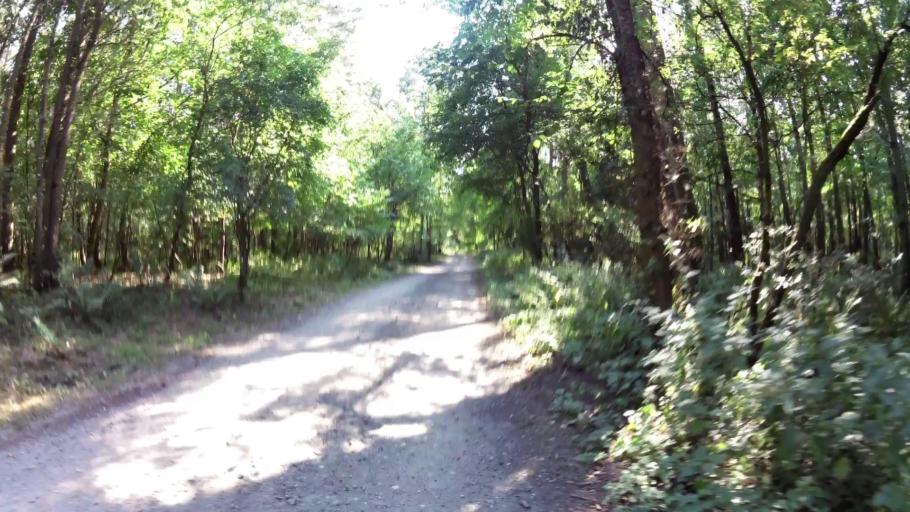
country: PL
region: West Pomeranian Voivodeship
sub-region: Powiat gryfinski
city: Moryn
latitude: 52.8669
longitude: 14.4265
